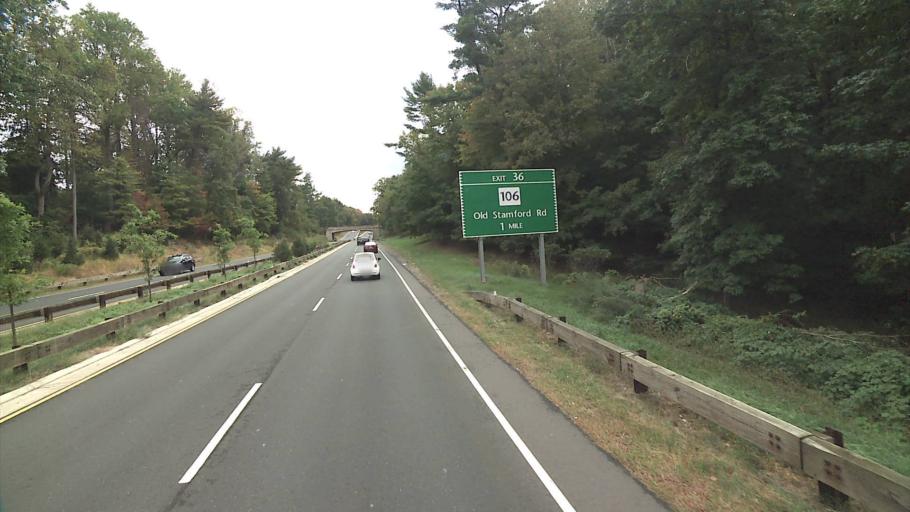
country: US
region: Connecticut
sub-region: Fairfield County
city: North Stamford
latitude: 41.1188
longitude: -73.5202
